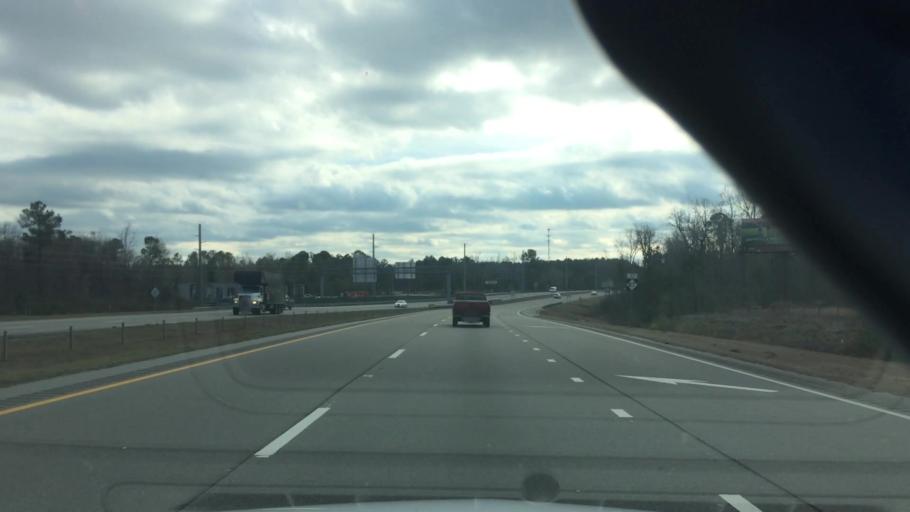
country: US
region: North Carolina
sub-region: Brunswick County
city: Leland
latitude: 34.1842
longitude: -78.0826
